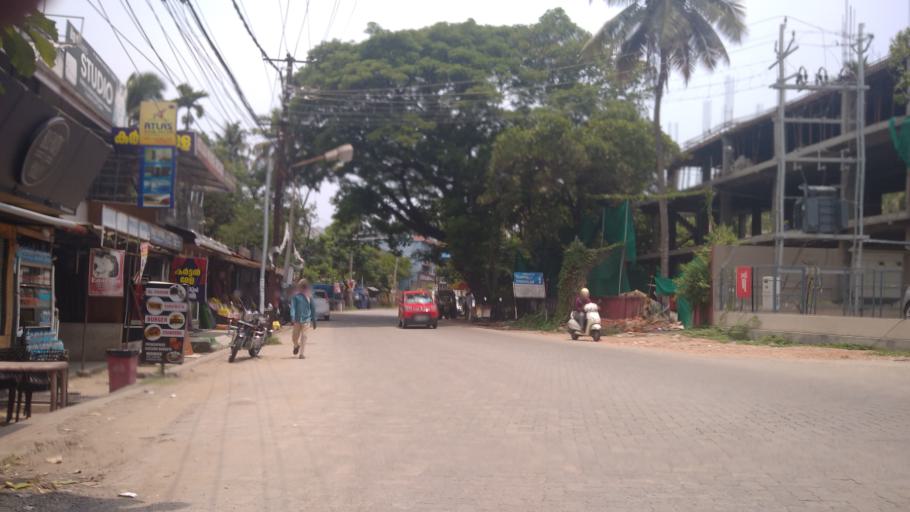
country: IN
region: Kerala
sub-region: Ernakulam
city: Elur
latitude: 10.0331
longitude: 76.3250
